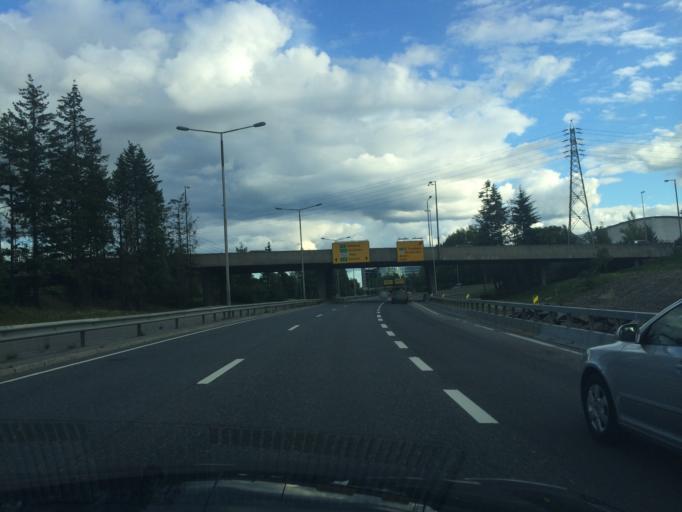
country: NO
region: Oslo
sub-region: Oslo
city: Oslo
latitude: 59.9234
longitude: 10.8073
